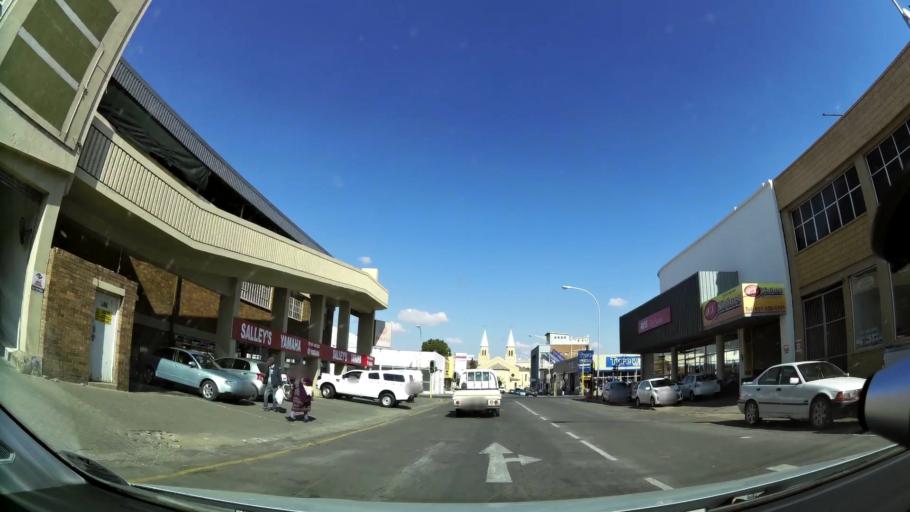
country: ZA
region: Orange Free State
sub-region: Mangaung Metropolitan Municipality
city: Bloemfontein
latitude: -29.1140
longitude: 26.2228
